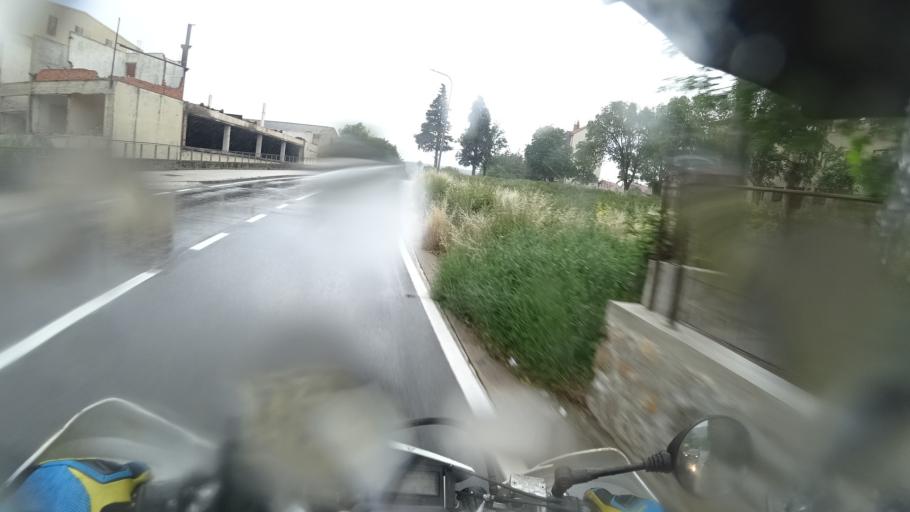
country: HR
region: Sibensko-Kniniska
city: Knin
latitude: 44.0391
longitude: 16.2056
